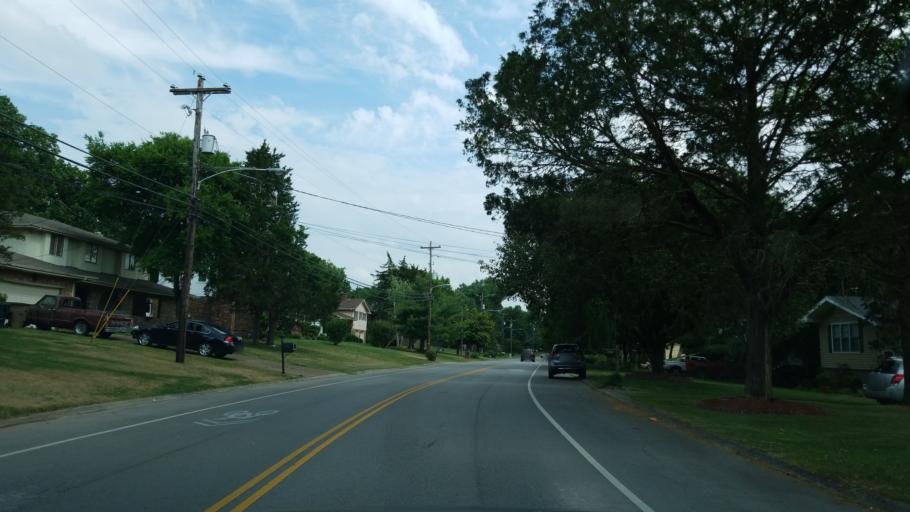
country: US
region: Tennessee
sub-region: Rutherford County
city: La Vergne
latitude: 36.0868
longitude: -86.6138
